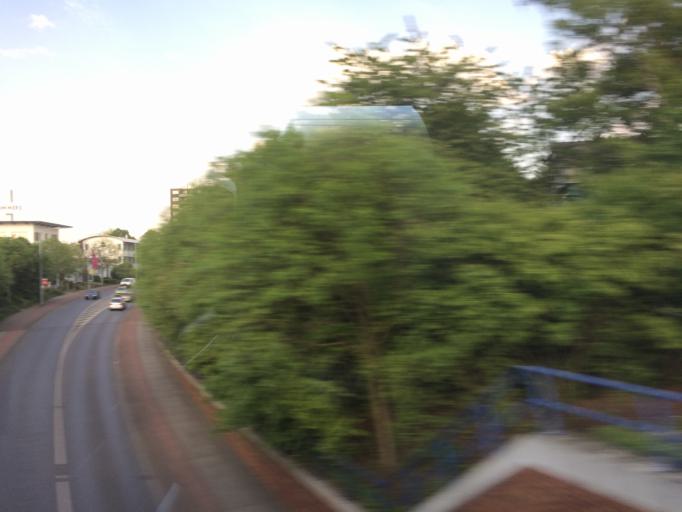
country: DE
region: North Rhine-Westphalia
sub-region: Regierungsbezirk Dusseldorf
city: Hochfeld
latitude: 51.3711
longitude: 6.7773
